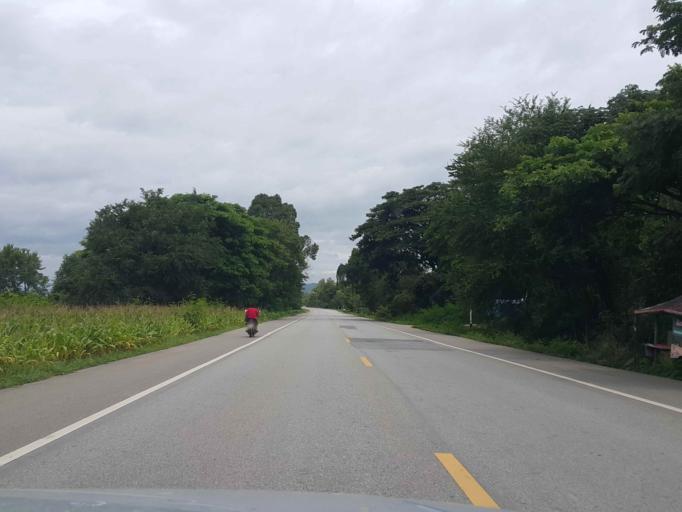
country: TH
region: Lamphun
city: Li
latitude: 17.7447
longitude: 99.0239
